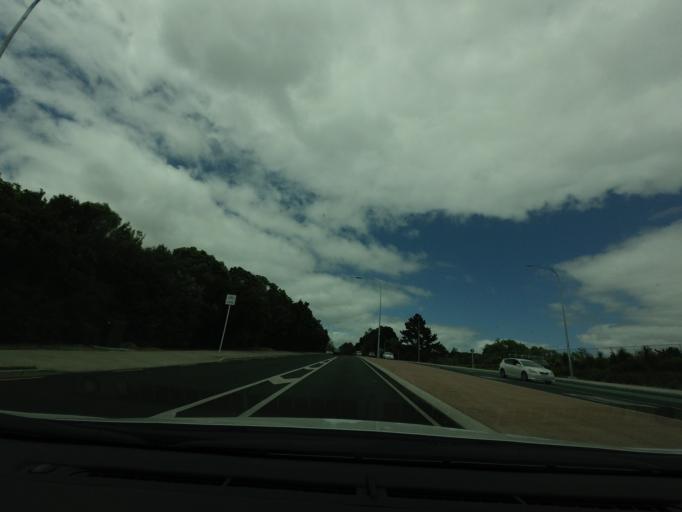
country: NZ
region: Auckland
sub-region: Auckland
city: Auckland
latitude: -36.8694
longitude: 174.7258
